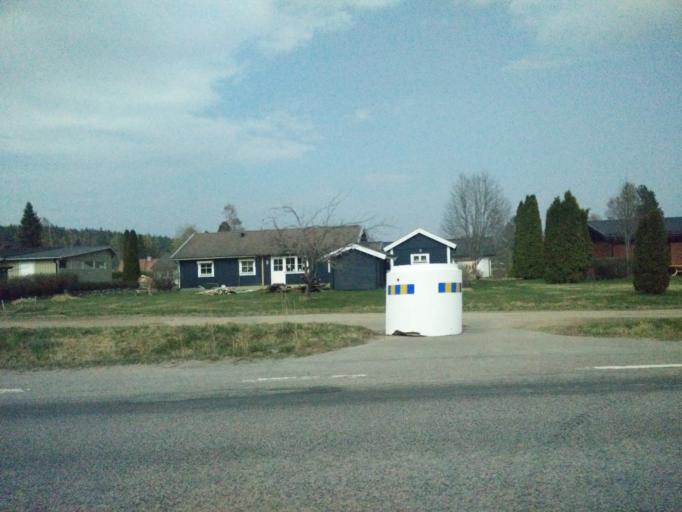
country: SE
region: Vaermland
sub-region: Munkfors Kommun
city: Munkfors
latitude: 59.8313
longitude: 13.5167
